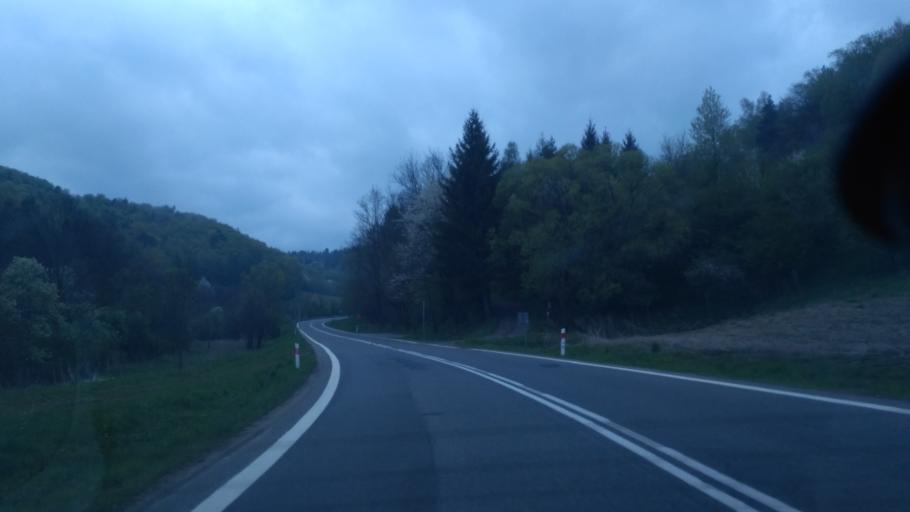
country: PL
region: Subcarpathian Voivodeship
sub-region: Powiat sanocki
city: Zagorz
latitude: 49.5389
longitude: 22.3039
